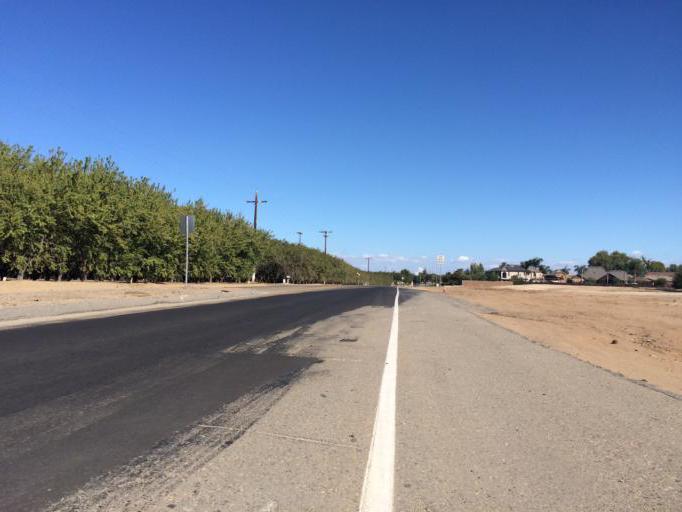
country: US
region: California
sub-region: Fresno County
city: Clovis
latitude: 36.8665
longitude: -119.6996
